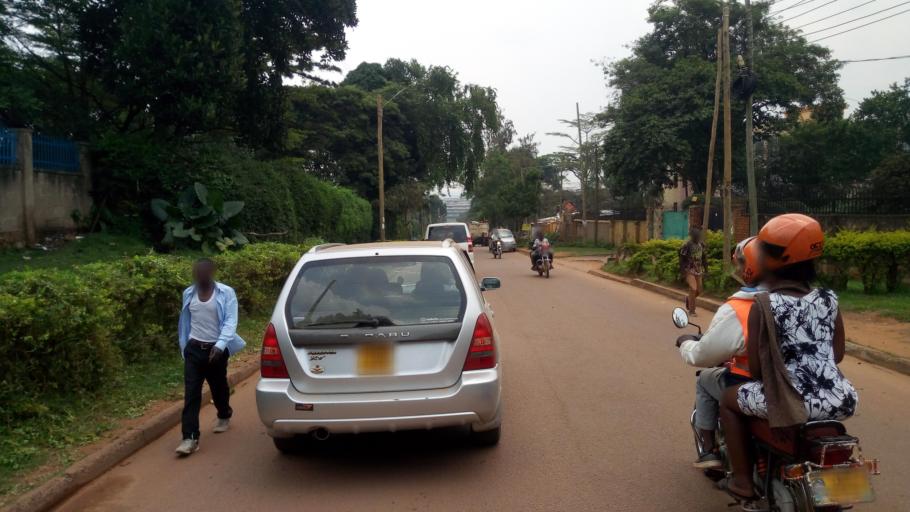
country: UG
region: Central Region
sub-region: Kampala District
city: Kampala
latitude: 0.3183
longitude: 32.6210
